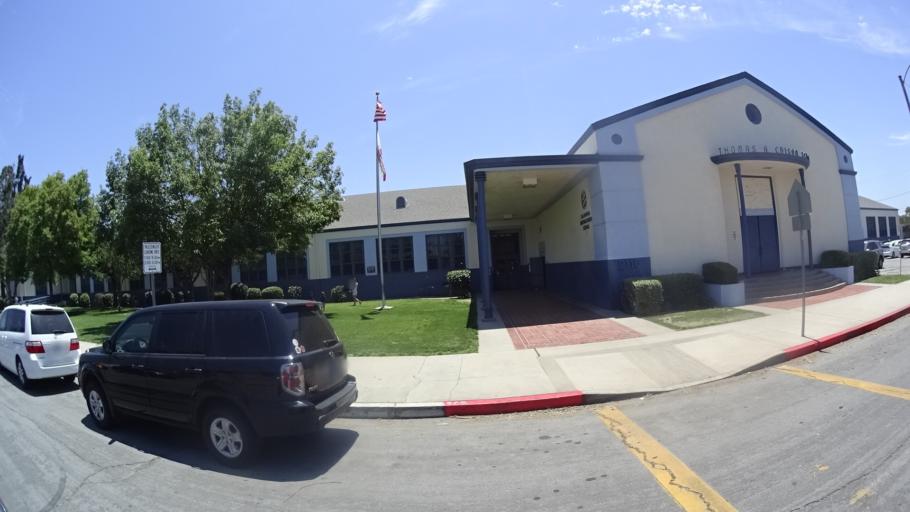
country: US
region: California
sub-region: Los Angeles County
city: Burbank
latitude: 34.1783
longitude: -118.3342
